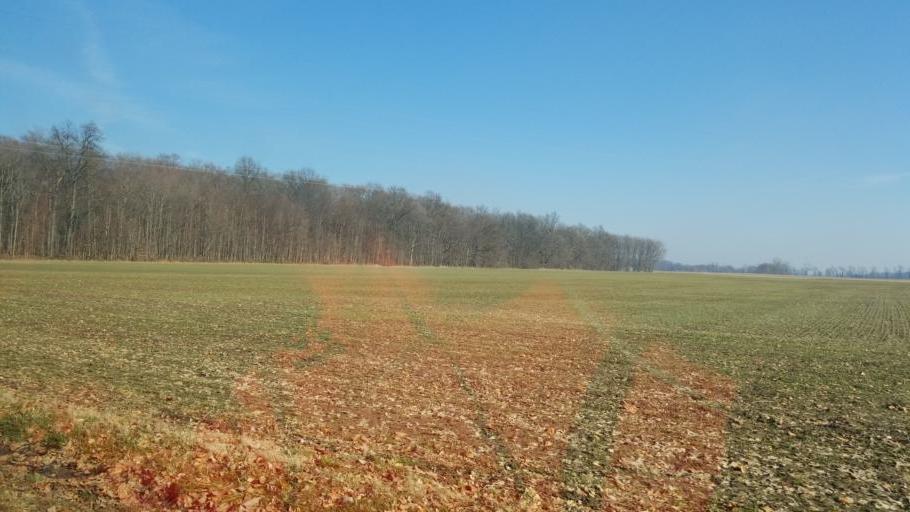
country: US
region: Ohio
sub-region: Seneca County
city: Tiffin
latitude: 41.0160
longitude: -83.0741
